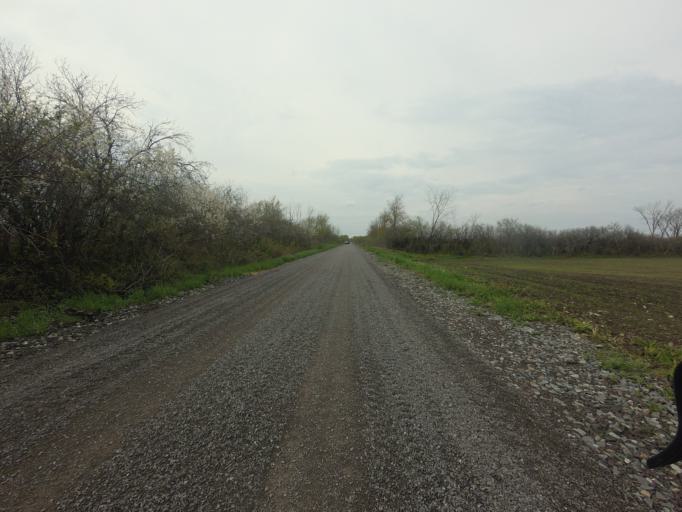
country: CA
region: Ontario
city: Carleton Place
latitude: 45.1937
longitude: -76.1637
